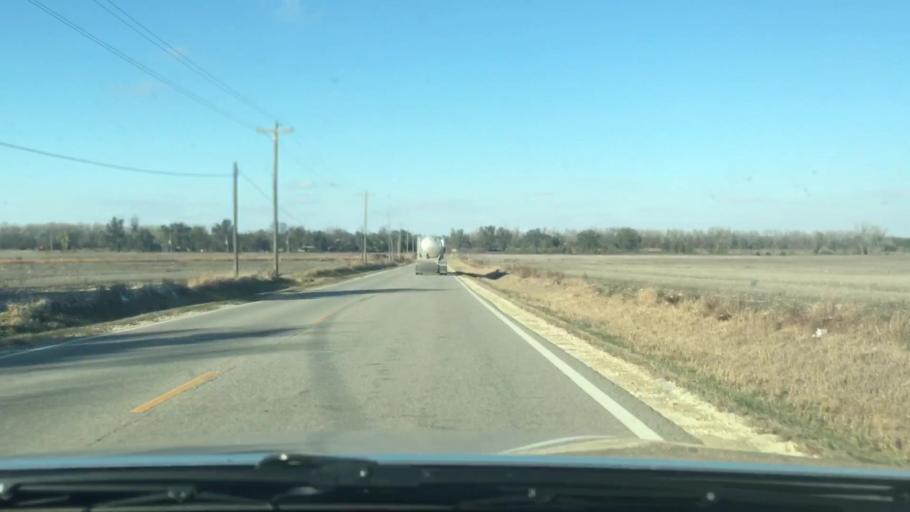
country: US
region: Kansas
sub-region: Rice County
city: Sterling
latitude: 38.1621
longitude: -98.2067
